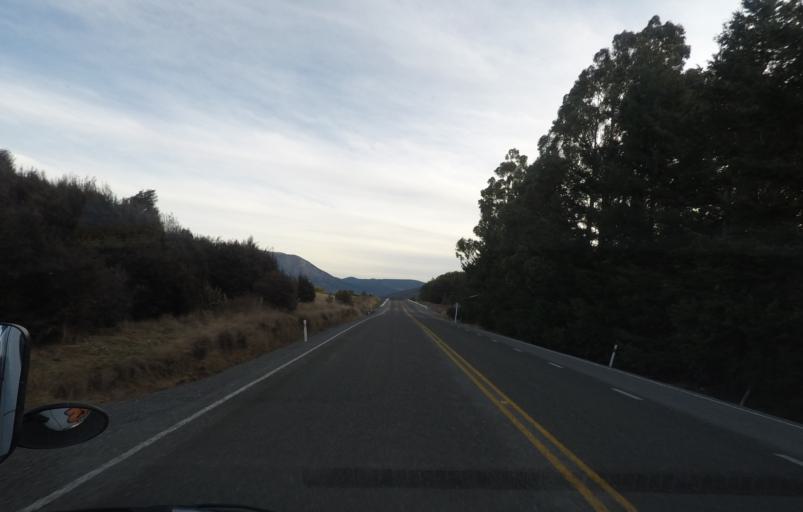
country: NZ
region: Tasman
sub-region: Tasman District
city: Wakefield
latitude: -41.7856
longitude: 172.8926
